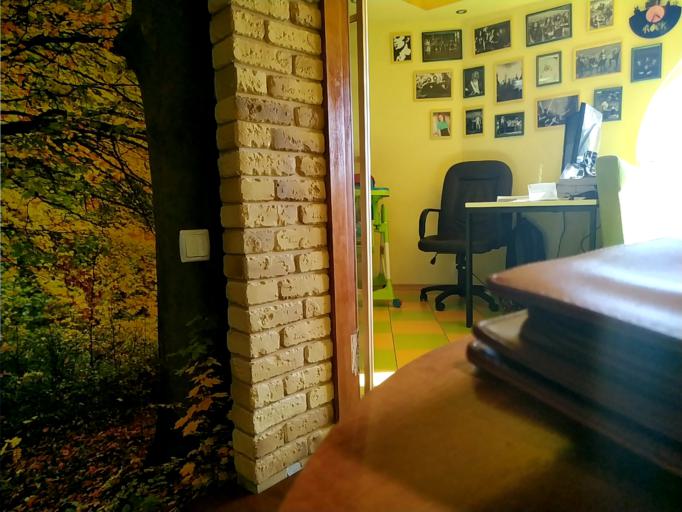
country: RU
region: Vologda
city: Nelazskoye
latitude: 59.4247
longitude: 37.6079
